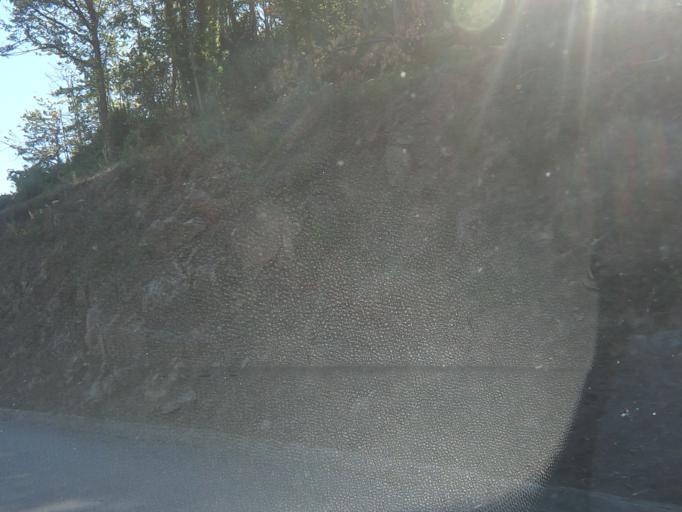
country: PT
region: Vila Real
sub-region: Santa Marta de Penaguiao
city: Santa Marta de Penaguiao
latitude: 41.2406
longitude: -7.8045
